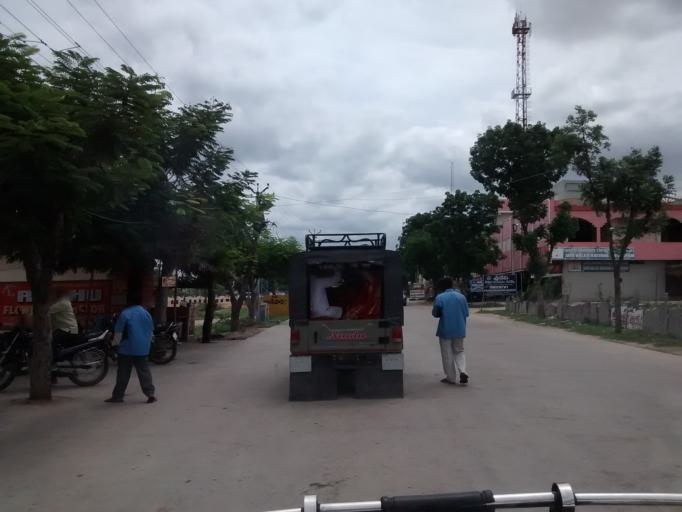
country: IN
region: Andhra Pradesh
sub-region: Chittoor
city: Chittoor
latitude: 13.2771
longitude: 79.0403
